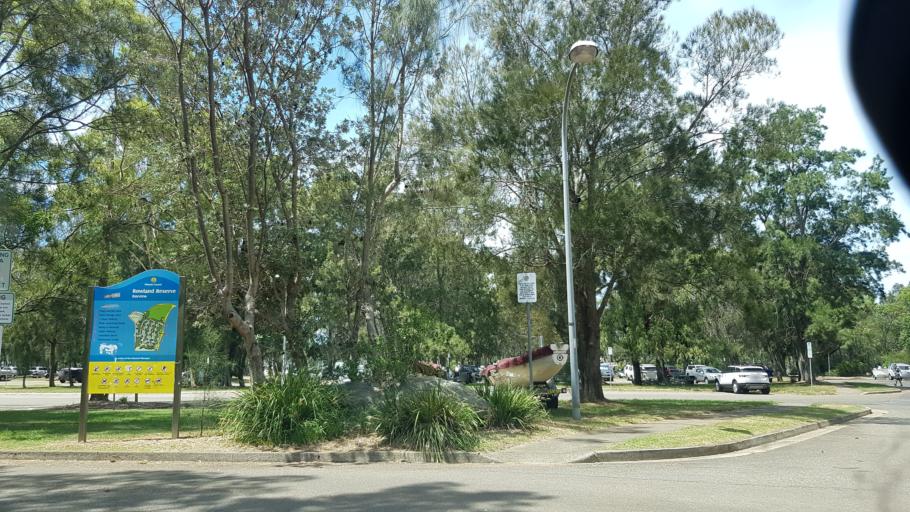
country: AU
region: New South Wales
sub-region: Pittwater
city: Bay View
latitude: -33.6626
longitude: 151.3019
